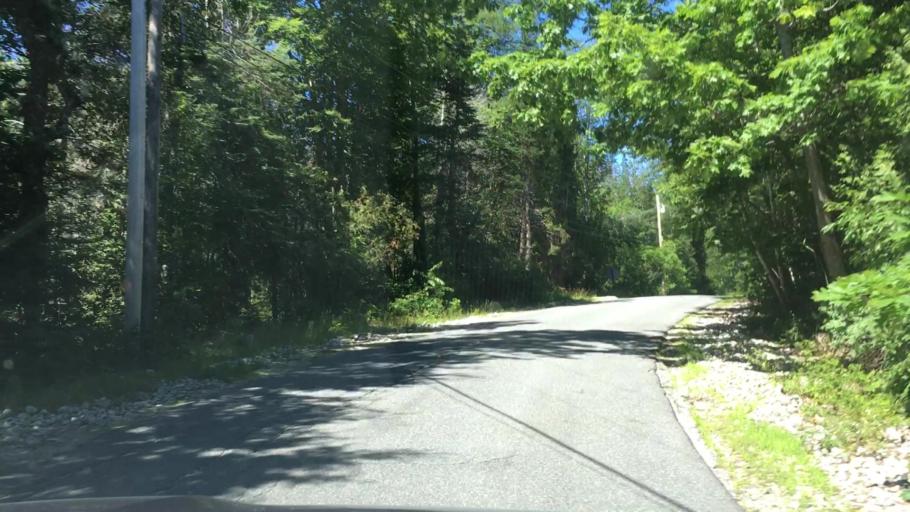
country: US
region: Maine
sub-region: Hancock County
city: Sedgwick
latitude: 44.3159
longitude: -68.6173
